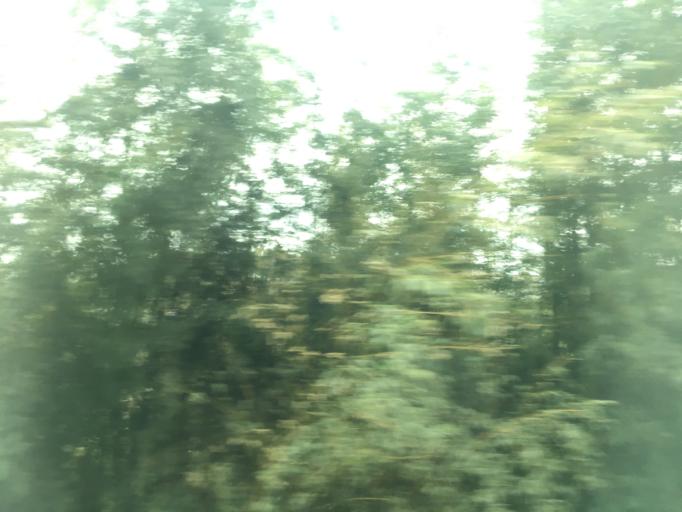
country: JP
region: Chiba
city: Narita
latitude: 35.7844
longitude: 140.3066
